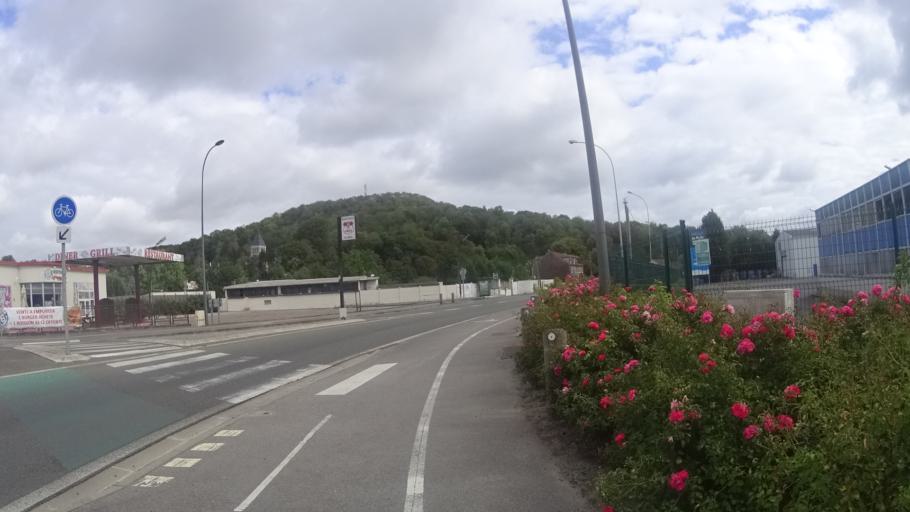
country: FR
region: Picardie
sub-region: Departement de l'Oise
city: Clairoix
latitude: 49.4383
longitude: 2.8499
